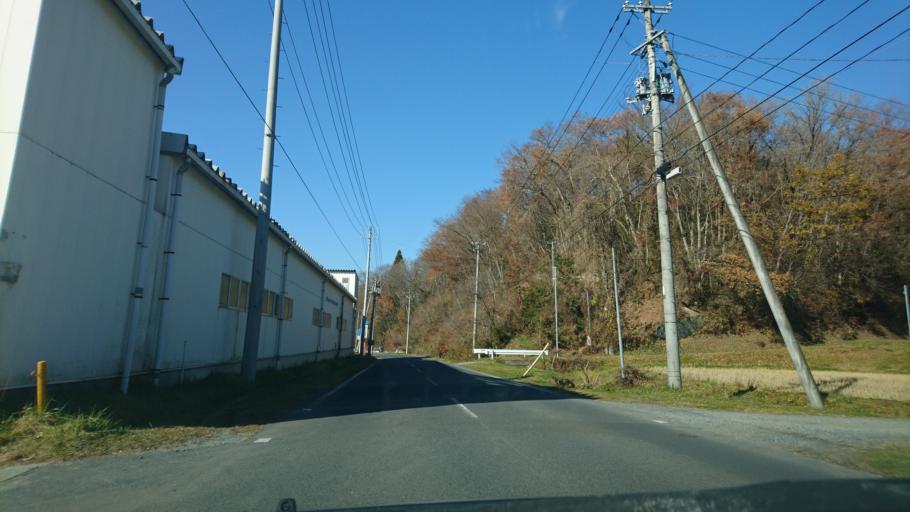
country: JP
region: Iwate
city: Ichinoseki
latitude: 38.9096
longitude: 141.3523
